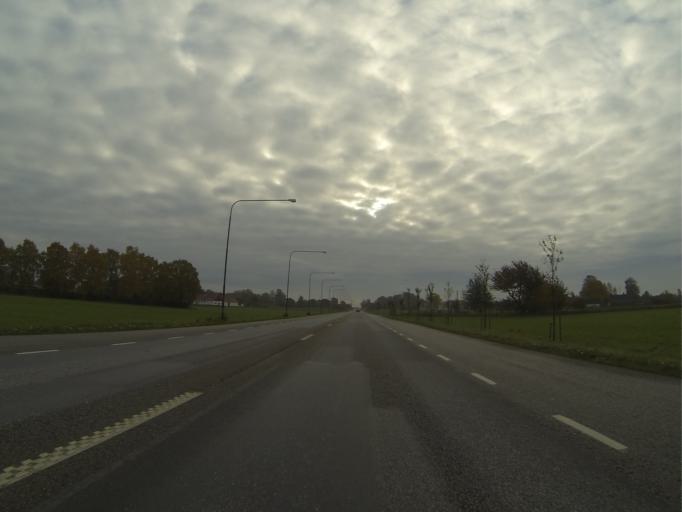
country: SE
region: Skane
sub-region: Tomelilla Kommun
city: Tomelilla
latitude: 55.5542
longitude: 13.9343
